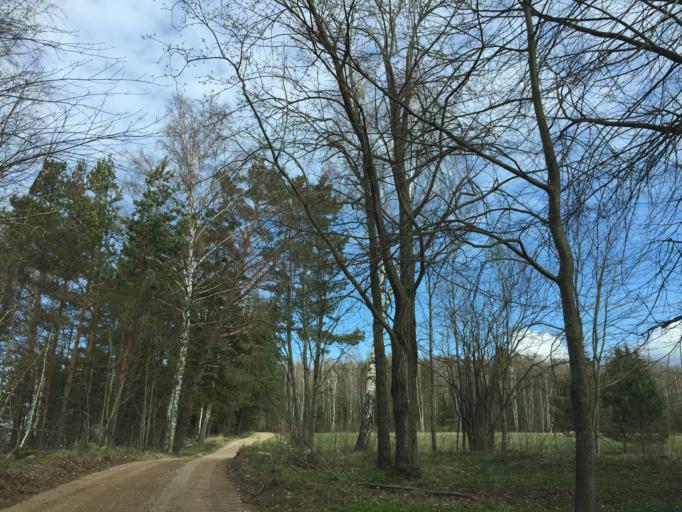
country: LV
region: Salacgrivas
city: Salacgriva
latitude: 57.5954
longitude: 24.3735
